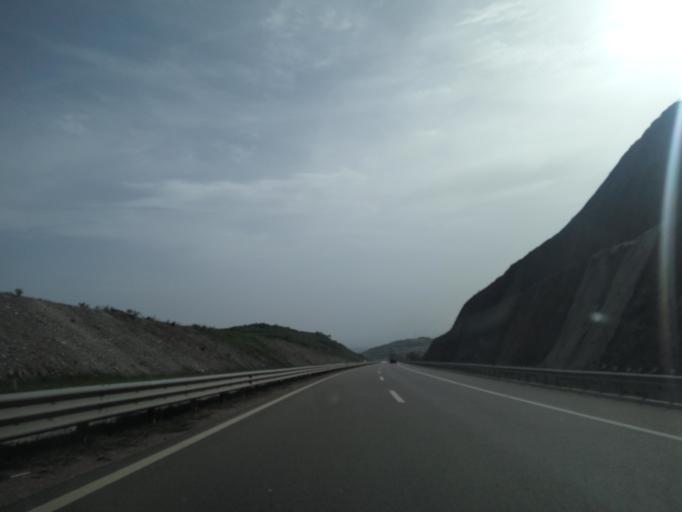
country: XK
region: Prizren
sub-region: Komuna e Therandes
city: Peqan
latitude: 42.3924
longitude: 20.8575
